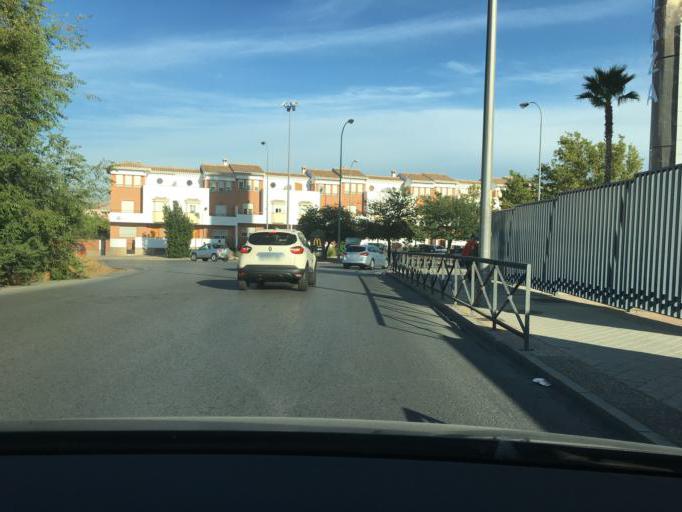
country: ES
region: Andalusia
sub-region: Provincia de Granada
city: Huetor Vega
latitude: 37.1560
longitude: -3.5850
